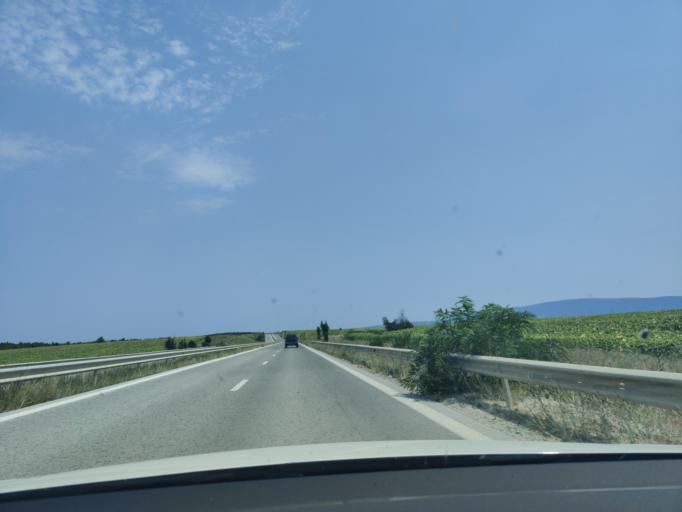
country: BG
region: Montana
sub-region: Obshtina Montana
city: Montana
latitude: 43.4300
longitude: 23.1796
